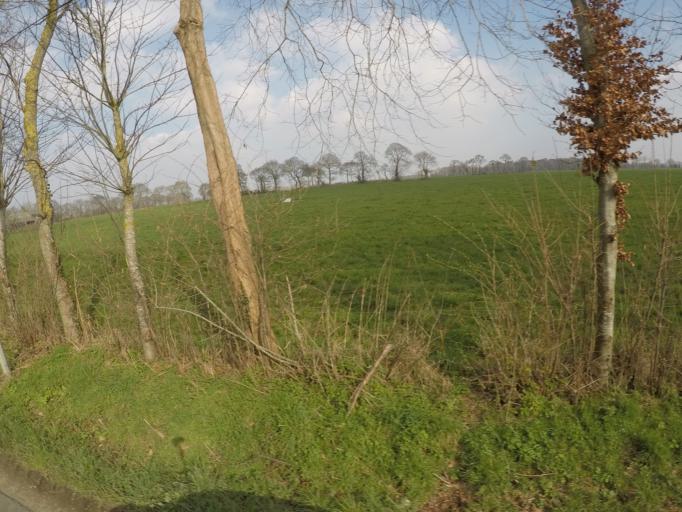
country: FR
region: Brittany
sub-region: Departement des Cotes-d'Armor
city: Goudelin
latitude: 48.6144
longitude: -3.0380
